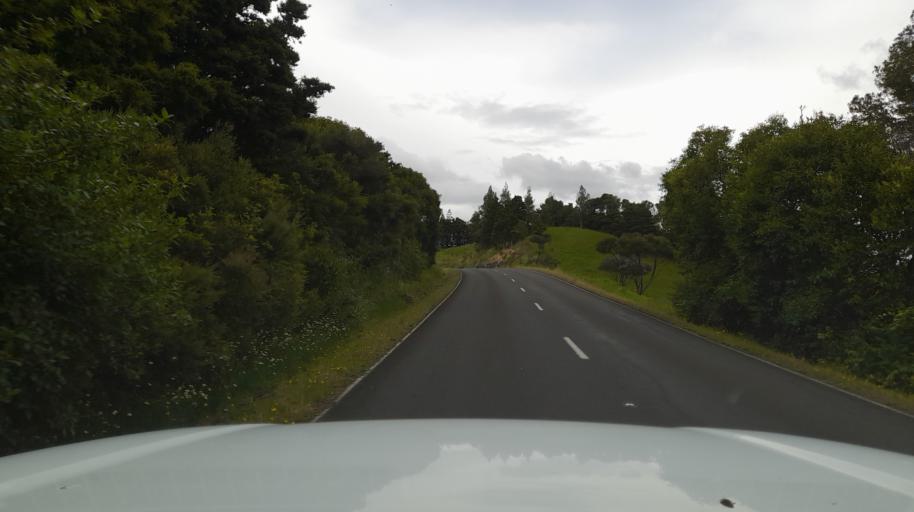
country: NZ
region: Northland
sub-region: Far North District
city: Kaitaia
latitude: -35.2780
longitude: 173.3698
